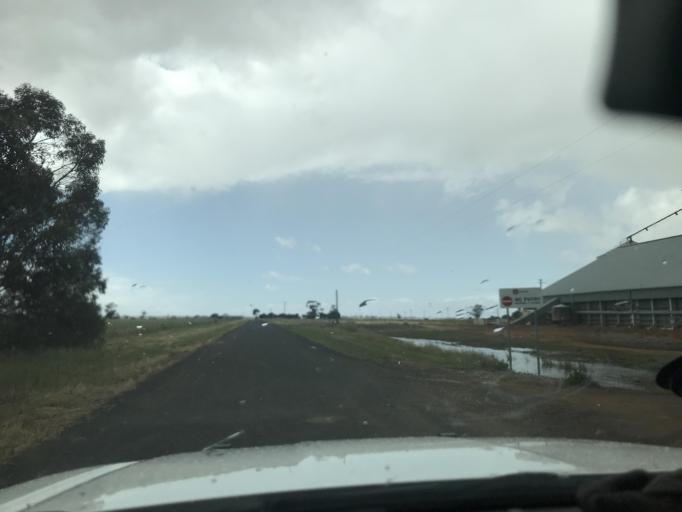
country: AU
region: South Australia
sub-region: Tatiara
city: Bordertown
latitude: -36.3743
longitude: 140.9860
